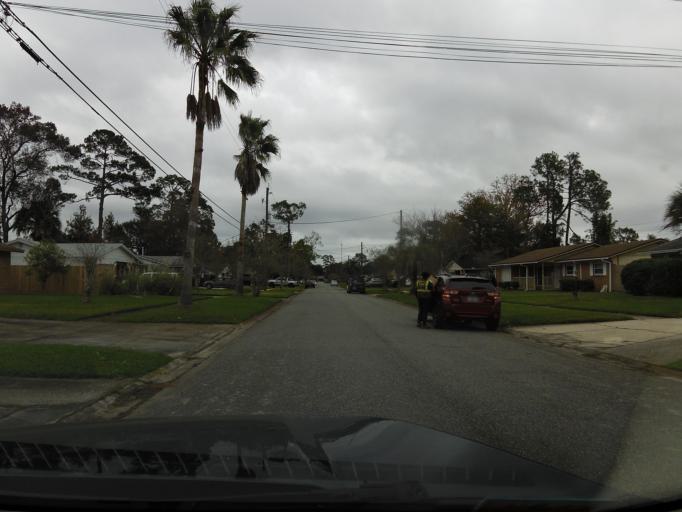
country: US
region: Florida
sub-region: Duval County
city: Jacksonville
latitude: 30.2854
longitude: -81.6099
